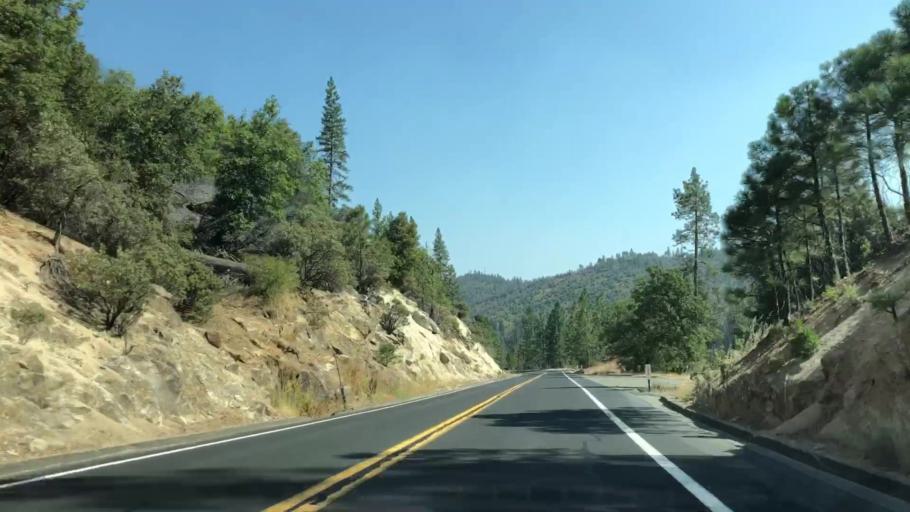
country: US
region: California
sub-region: Mariposa County
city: Midpines
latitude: 37.8182
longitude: -119.9510
